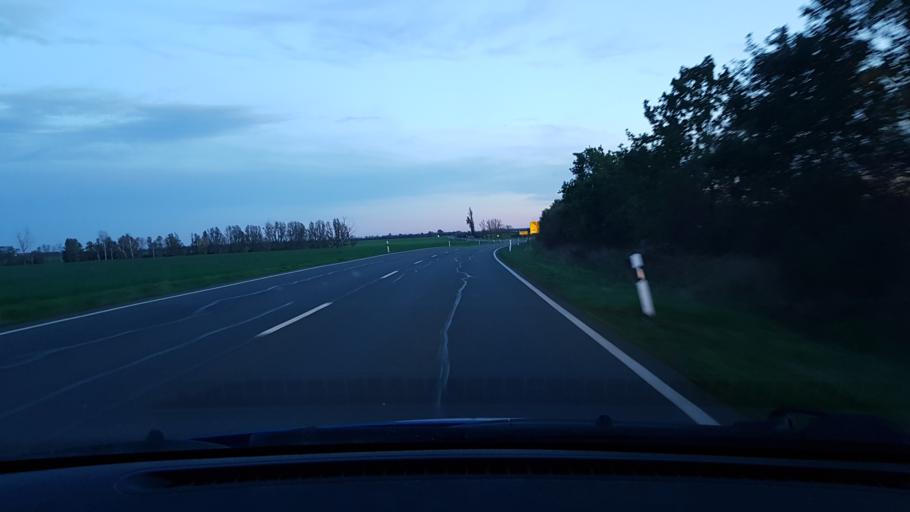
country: DE
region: Saxony-Anhalt
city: Zerbst
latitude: 52.0025
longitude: 12.0298
